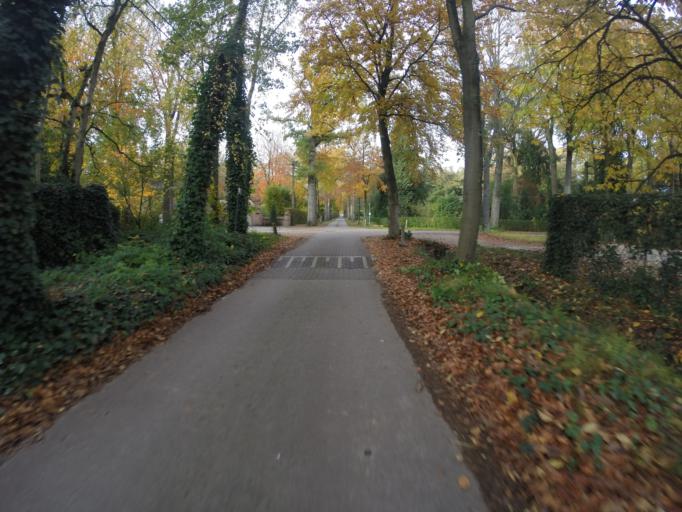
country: BE
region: Flanders
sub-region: Provincie Oost-Vlaanderen
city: Aalter
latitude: 51.0759
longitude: 3.4698
